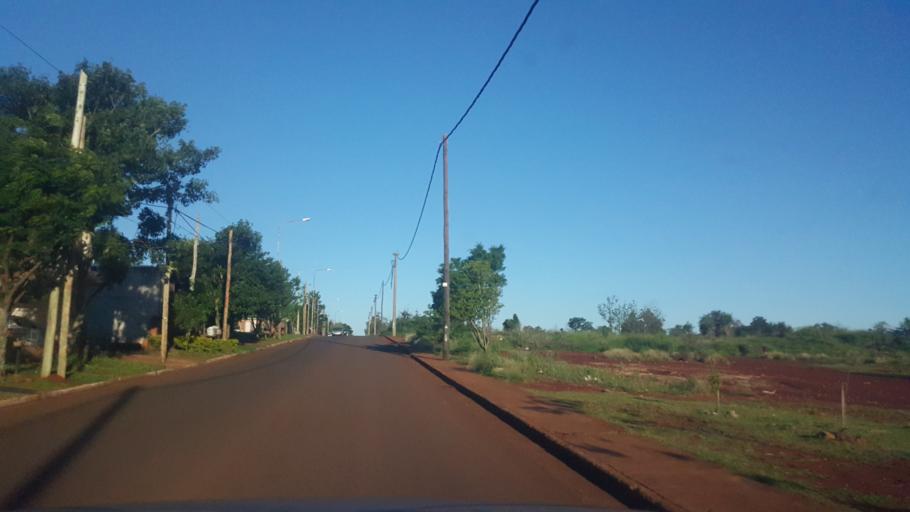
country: AR
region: Misiones
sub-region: Departamento de Capital
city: Posadas
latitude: -27.4243
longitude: -55.9497
